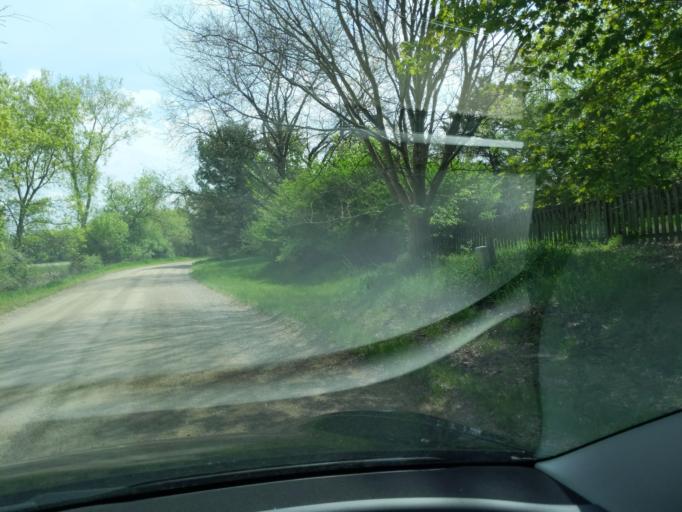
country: US
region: Michigan
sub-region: Ingham County
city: Stockbridge
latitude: 42.4420
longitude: -84.0733
